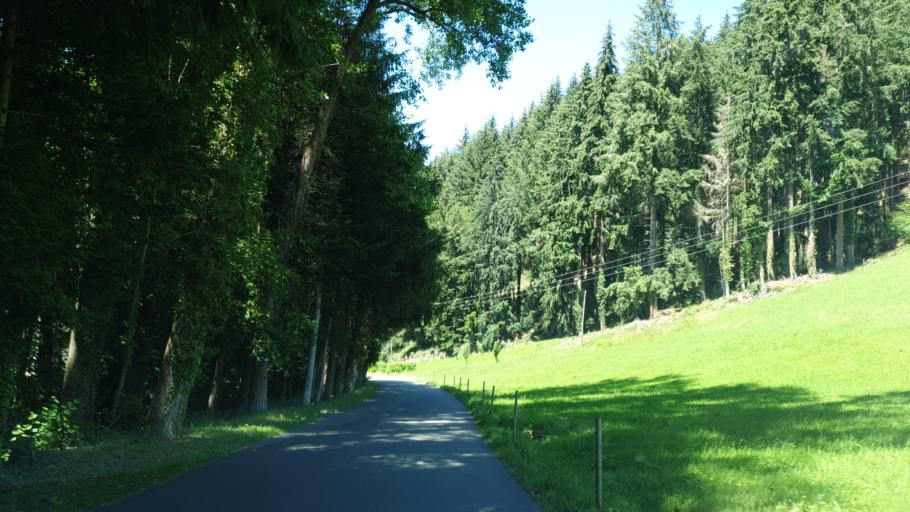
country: DE
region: Baden-Wuerttemberg
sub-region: Freiburg Region
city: Au
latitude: 47.9422
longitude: 7.8411
